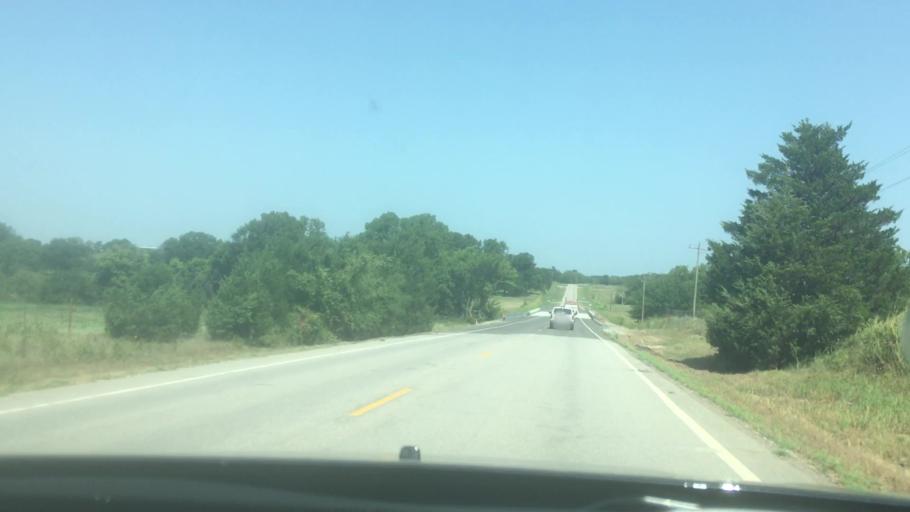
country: US
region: Oklahoma
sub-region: Bryan County
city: Durant
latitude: 34.1683
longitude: -96.4052
